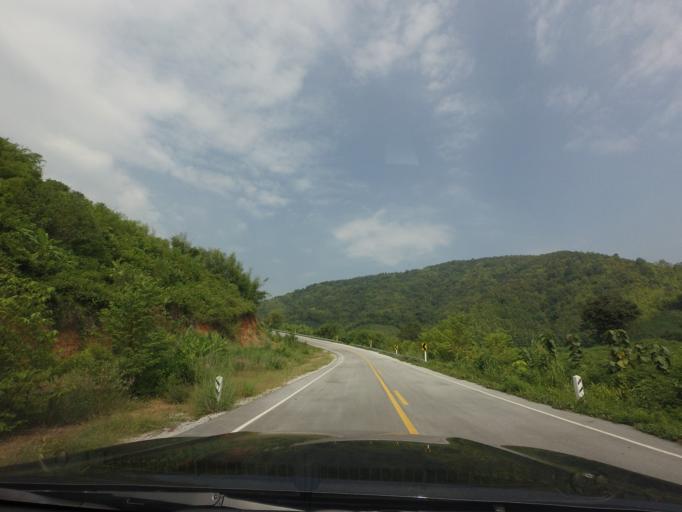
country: LA
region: Xiagnabouli
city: Muang Kenthao
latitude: 17.7747
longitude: 101.5237
